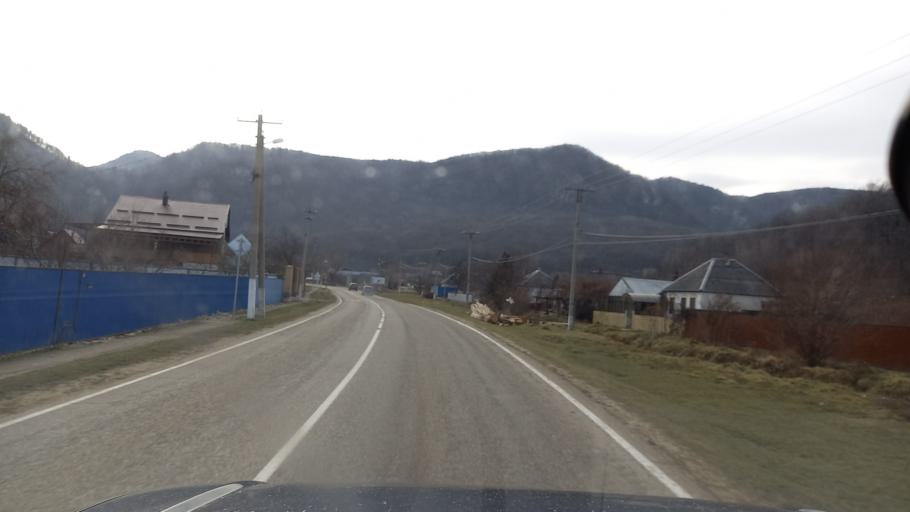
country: RU
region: Krasnodarskiy
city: Neftegorsk
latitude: 44.2333
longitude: 39.9019
